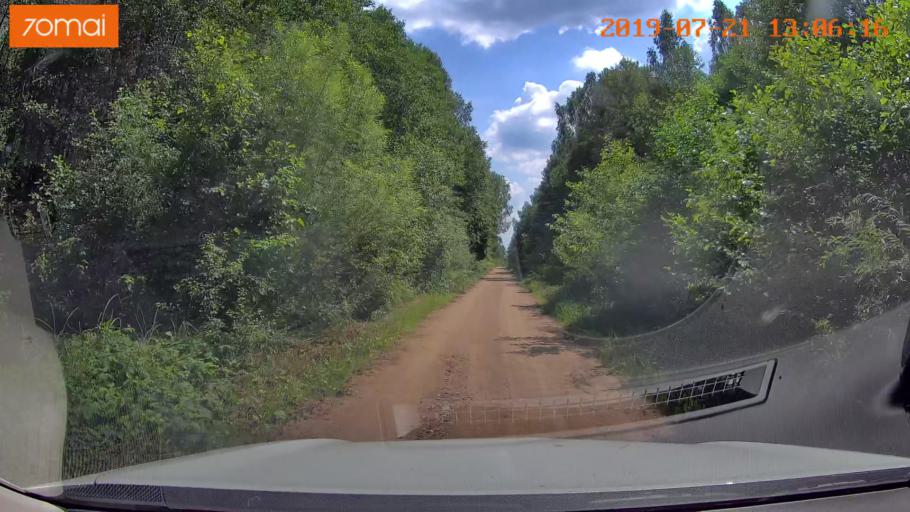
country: BY
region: Grodnenskaya
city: Lyubcha
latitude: 53.8299
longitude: 26.0406
